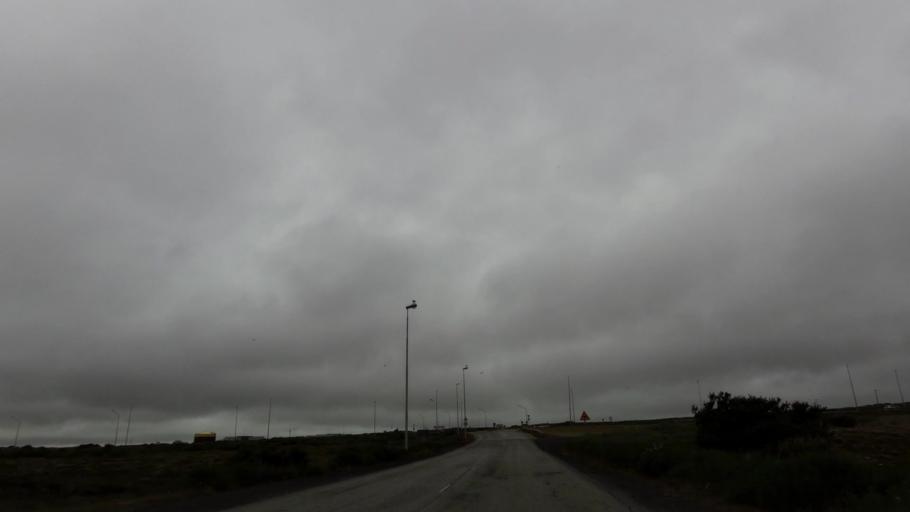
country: IS
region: Southern Peninsula
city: Reykjanesbaer
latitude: 63.9811
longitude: -22.5594
